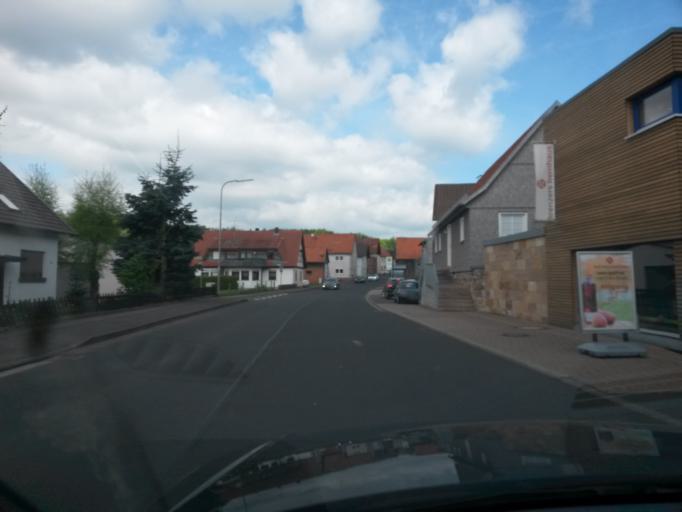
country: DE
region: Thuringia
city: Birx
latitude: 50.5245
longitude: 10.0155
